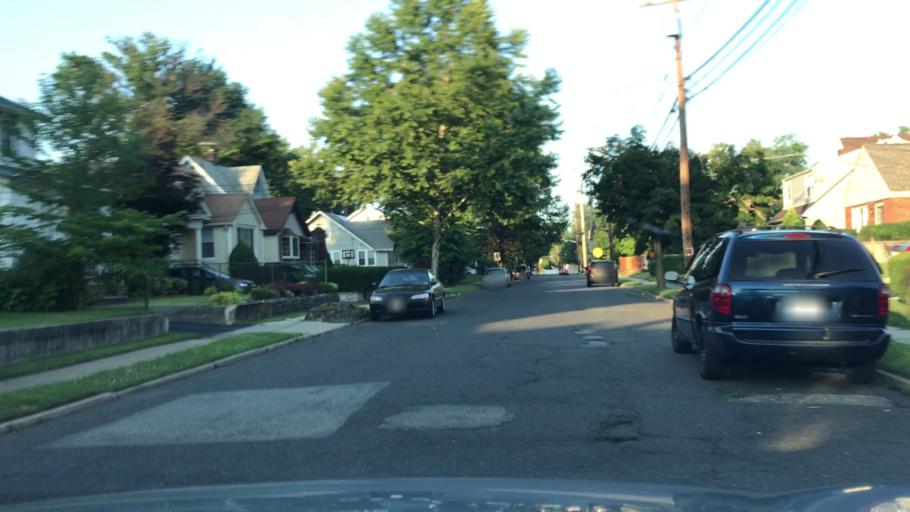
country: US
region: New Jersey
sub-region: Bergen County
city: Bergenfield
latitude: 40.9333
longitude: -73.9999
